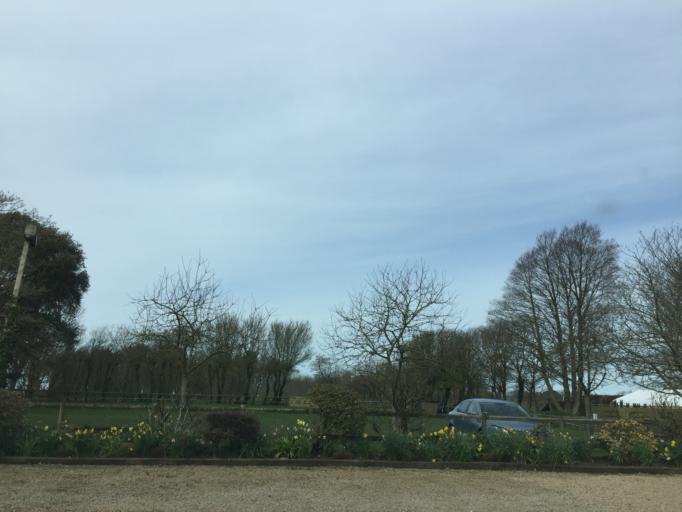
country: JE
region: St Helier
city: Saint Helier
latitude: 49.2457
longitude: -2.1686
